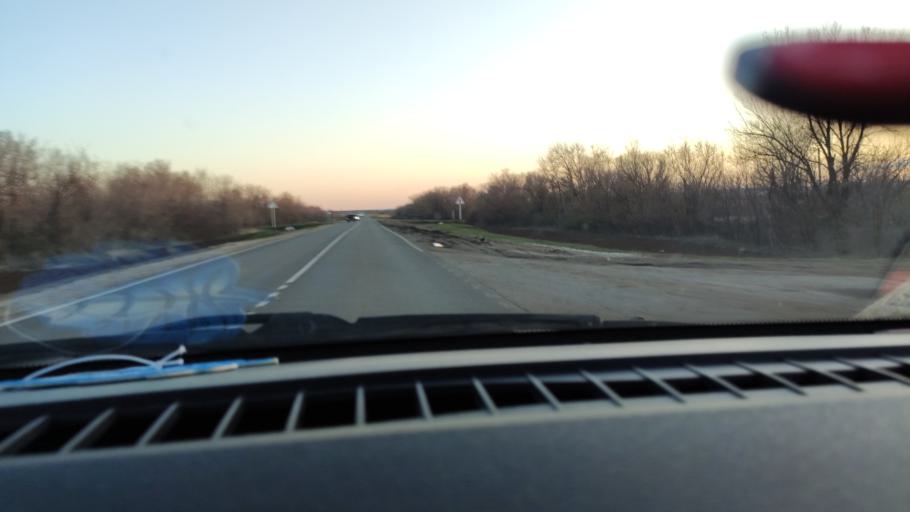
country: RU
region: Saratov
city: Privolzhskiy
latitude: 51.3159
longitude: 46.0191
